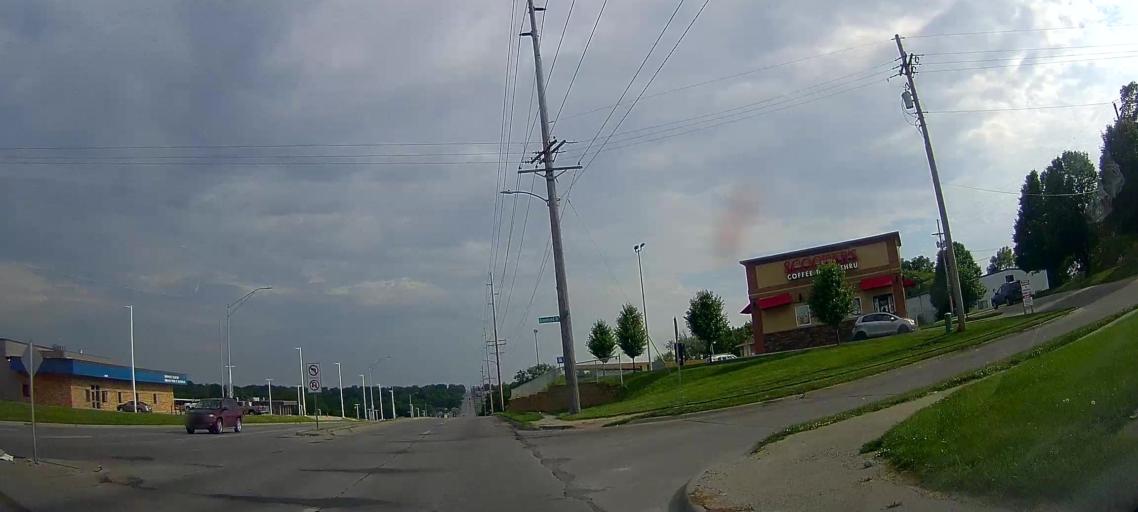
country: US
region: Nebraska
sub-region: Douglas County
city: Ralston
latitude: 41.2959
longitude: -96.0240
